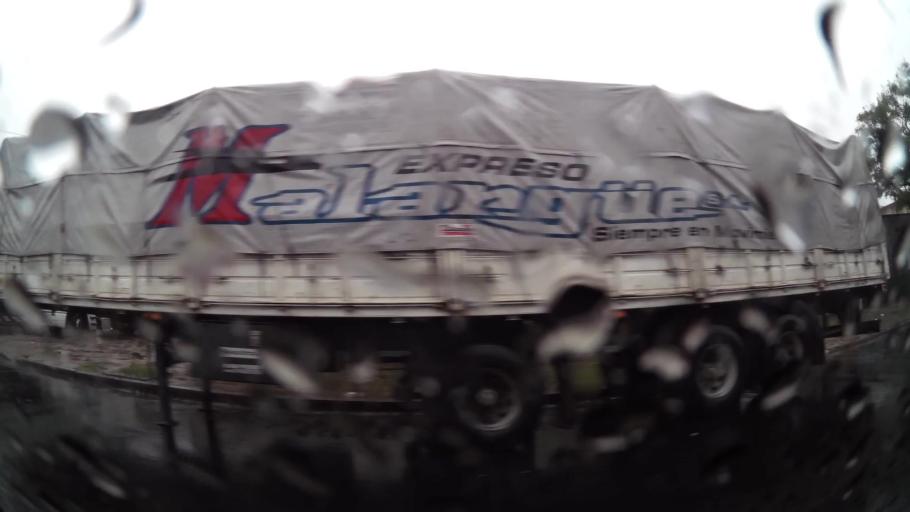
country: AR
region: Buenos Aires
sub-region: Partido de Avellaneda
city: Avellaneda
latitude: -34.6438
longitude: -58.3990
